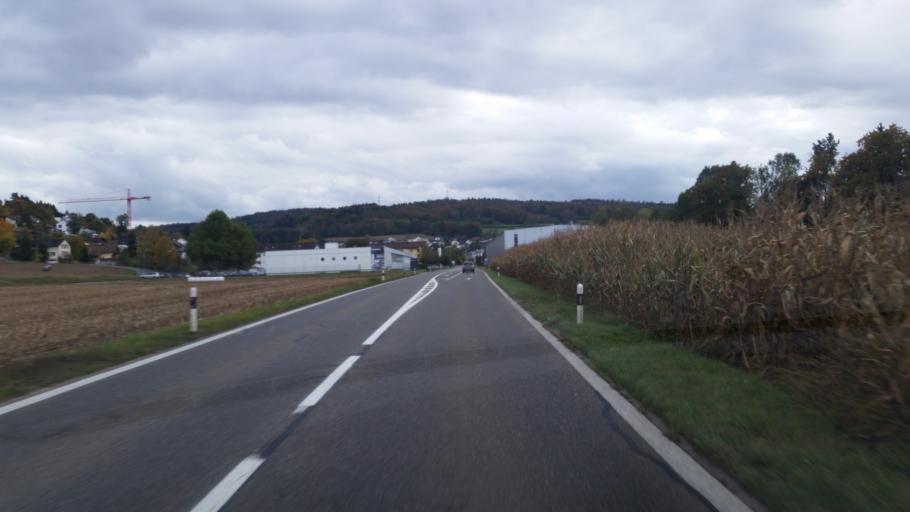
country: CH
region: Aargau
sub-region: Bezirk Zurzach
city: Oberendingen
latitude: 47.5444
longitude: 8.2900
